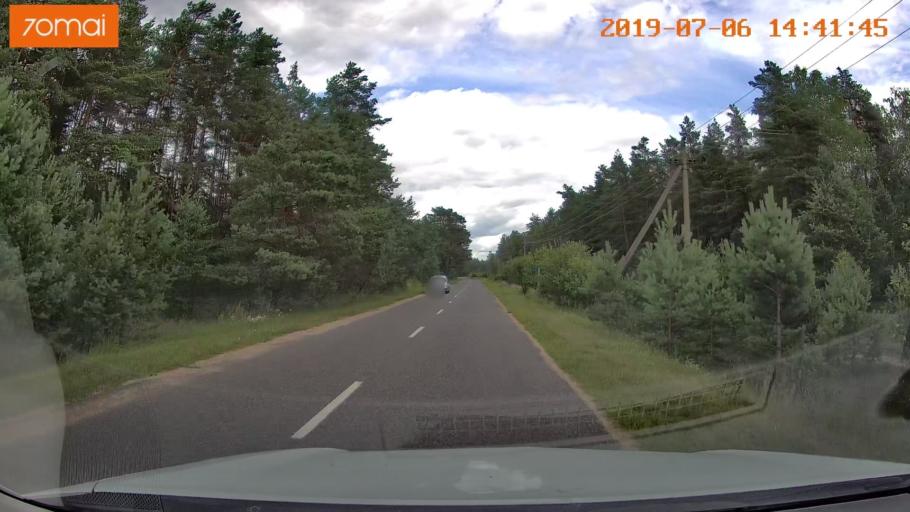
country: BY
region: Minsk
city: Ivyanyets
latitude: 53.9352
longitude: 26.6812
